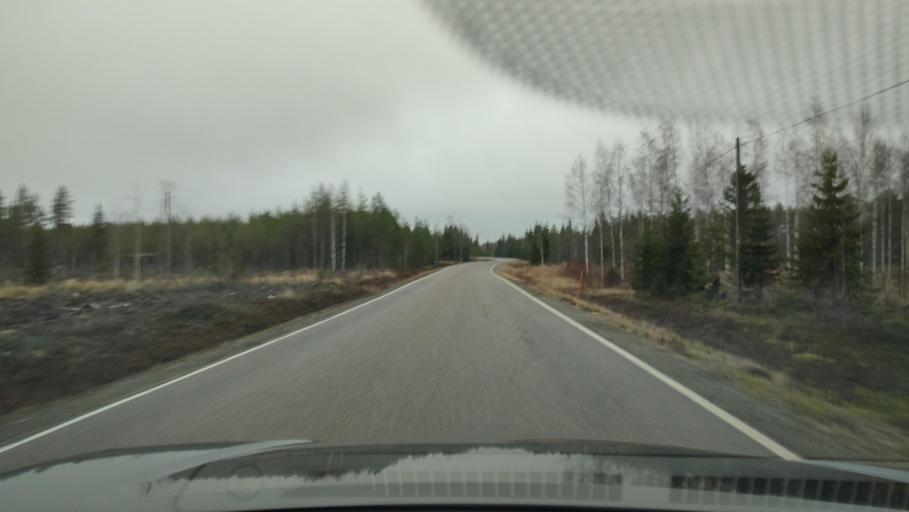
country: FI
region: Southern Ostrobothnia
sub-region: Suupohja
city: Isojoki
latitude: 62.2544
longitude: 22.0516
